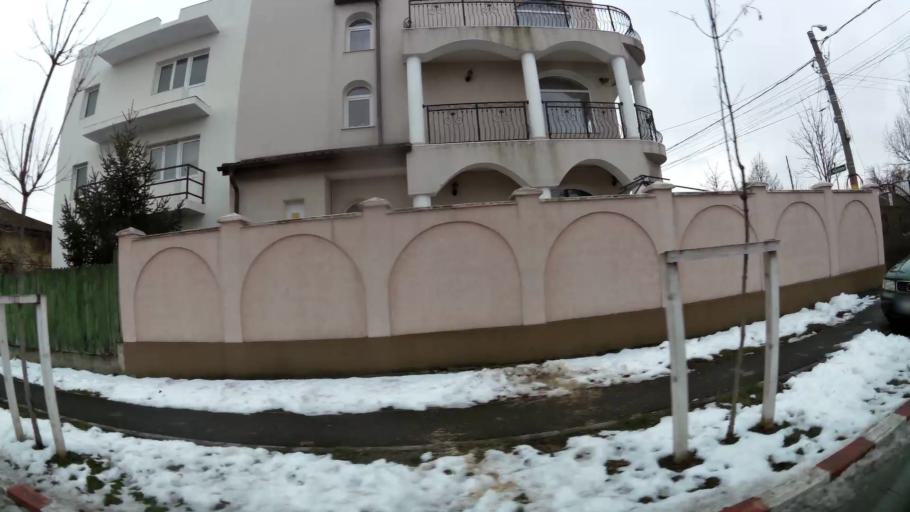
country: RO
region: Ilfov
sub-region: Voluntari City
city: Voluntari
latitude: 44.4875
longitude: 26.1740
